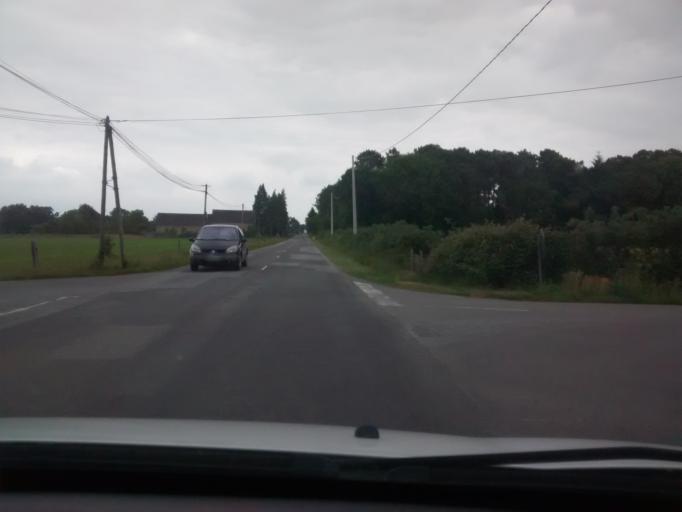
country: FR
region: Brittany
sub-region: Departement d'Ille-et-Vilaine
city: La Bouexiere
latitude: 48.1648
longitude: -1.4391
